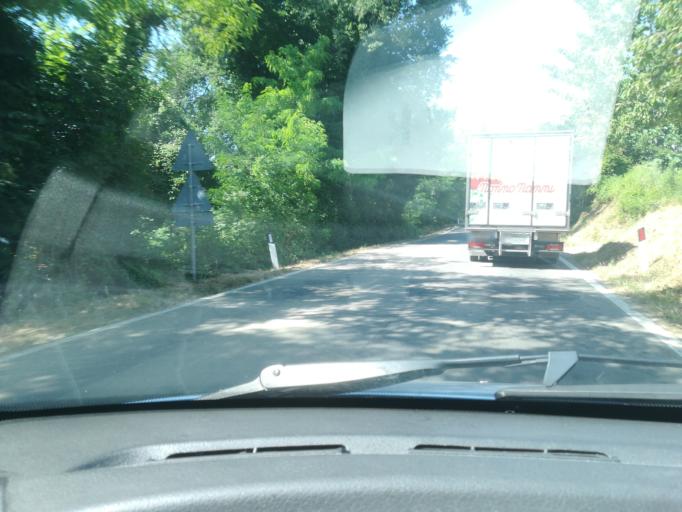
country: IT
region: The Marches
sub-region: Provincia di Macerata
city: Ripe San Ginesio
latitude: 43.1095
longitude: 13.3601
